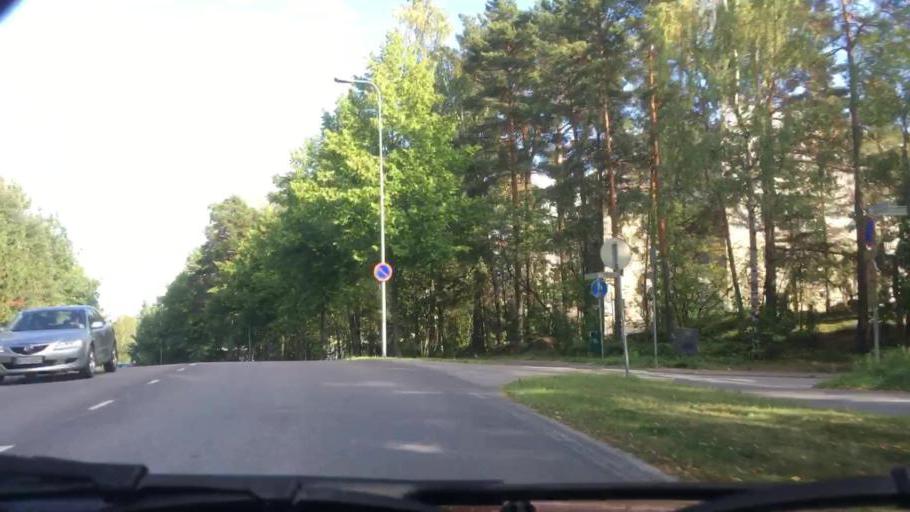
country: FI
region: Varsinais-Suomi
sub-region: Turku
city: Turku
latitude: 60.4648
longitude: 22.2375
